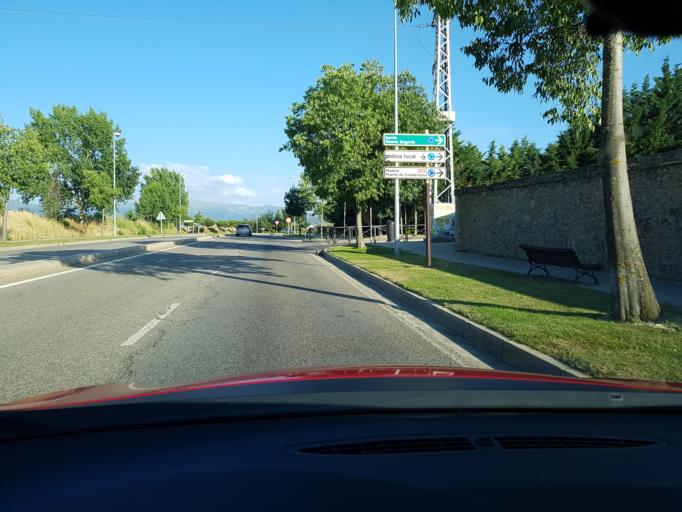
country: ES
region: Castille and Leon
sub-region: Provincia de Segovia
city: Segovia
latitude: 40.9374
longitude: -4.1007
